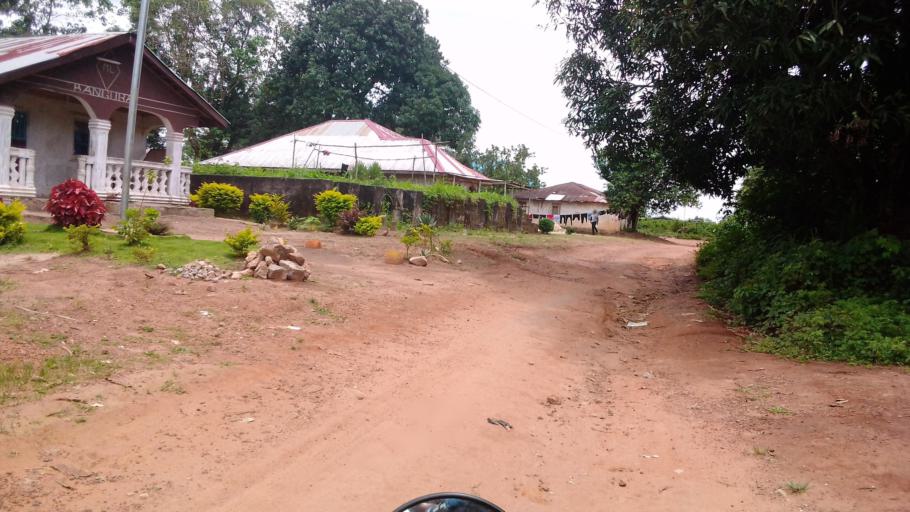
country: SL
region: Northern Province
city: Makeni
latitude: 8.8590
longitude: -12.0240
